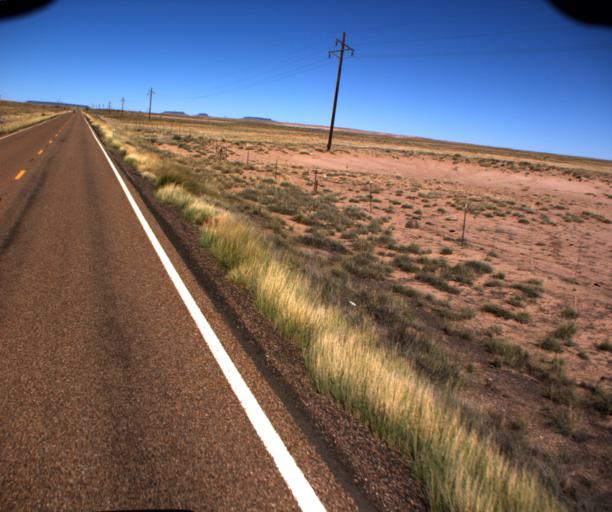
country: US
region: Arizona
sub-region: Navajo County
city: Holbrook
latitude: 35.1262
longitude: -110.0919
